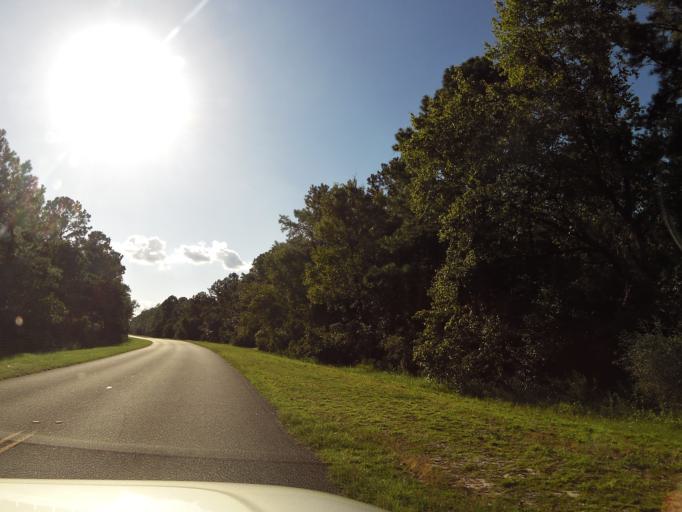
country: US
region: Florida
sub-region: Wakulla County
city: Crawfordville
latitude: 30.0644
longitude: -84.5096
